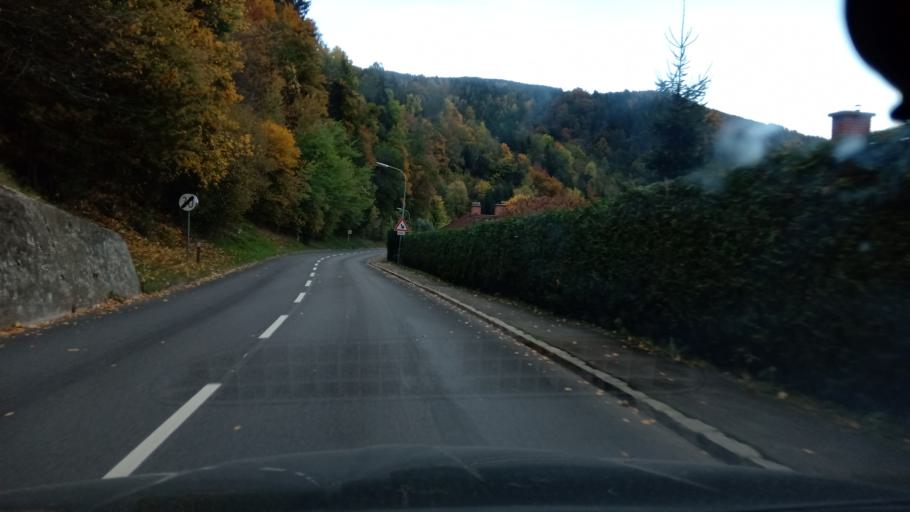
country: AT
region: Styria
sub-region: Politischer Bezirk Leoben
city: Proleb
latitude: 47.3909
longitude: 15.1237
